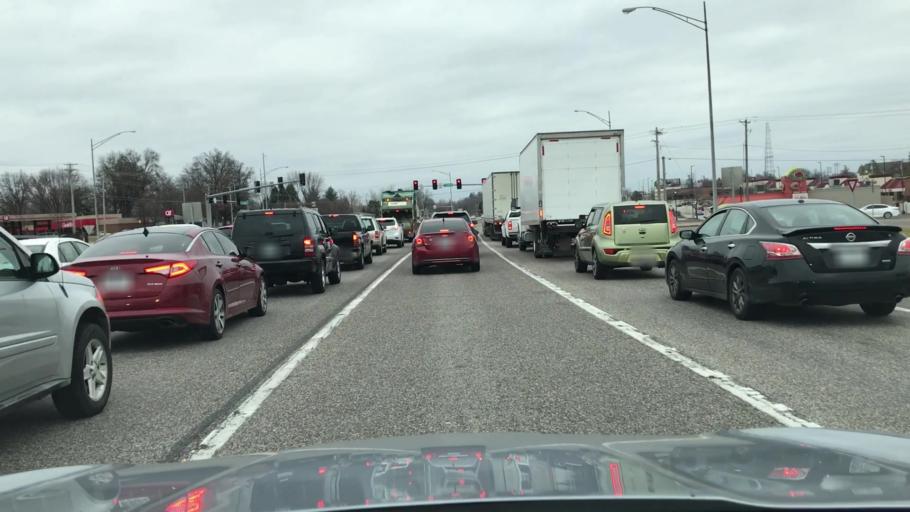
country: US
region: Missouri
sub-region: Saint Charles County
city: Saint Charles
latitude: 38.7678
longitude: -90.5244
